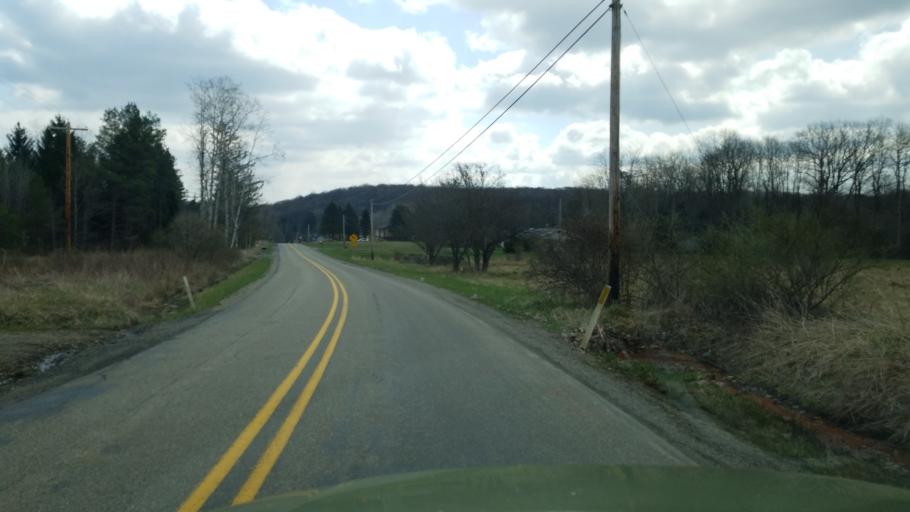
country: US
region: Pennsylvania
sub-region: Jefferson County
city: Brockway
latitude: 41.2735
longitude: -78.8342
